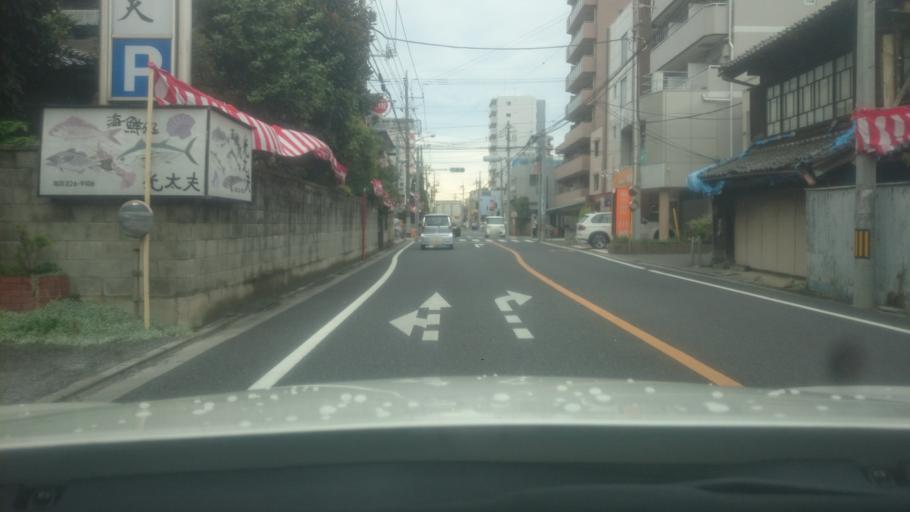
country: JP
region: Saitama
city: Kawagoe
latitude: 35.9067
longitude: 139.4867
